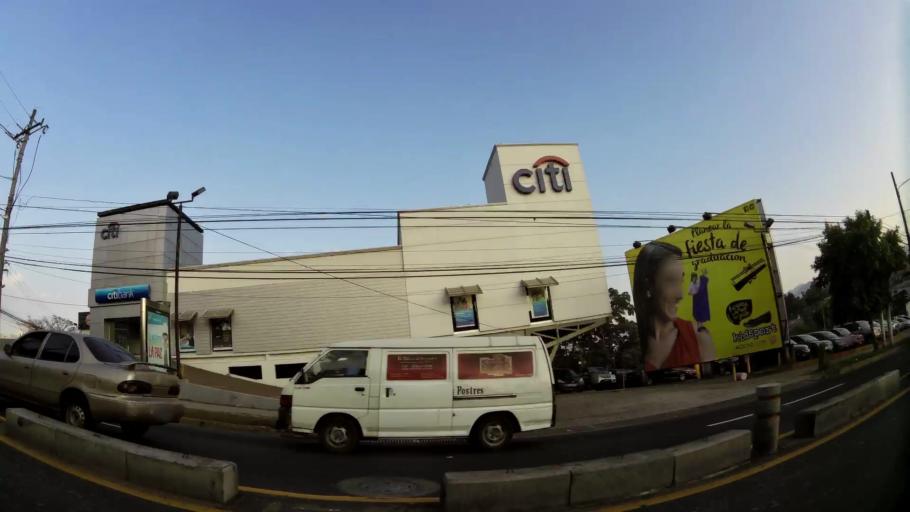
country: SV
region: La Libertad
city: Antiguo Cuscatlan
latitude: 13.7027
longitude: -89.2494
